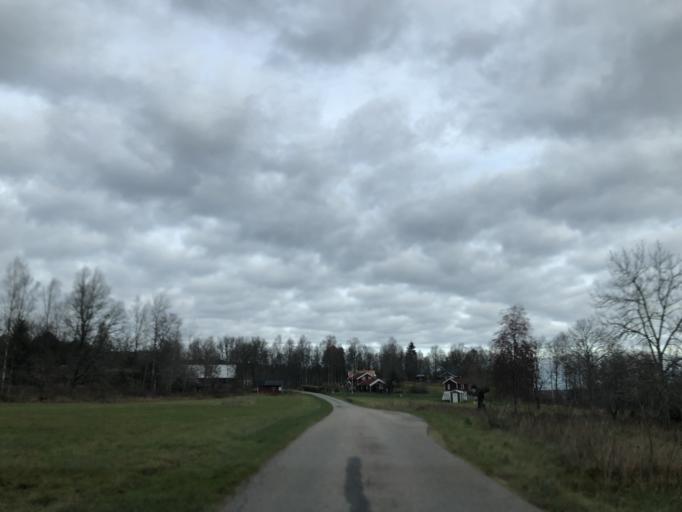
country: SE
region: Vaestra Goetaland
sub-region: Ulricehamns Kommun
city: Ulricehamn
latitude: 57.7313
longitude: 13.3700
